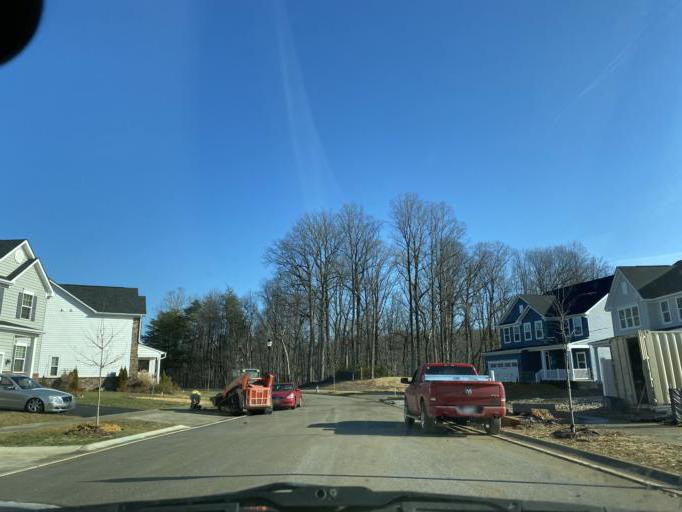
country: US
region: Maryland
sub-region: Montgomery County
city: Burtonsville
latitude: 39.0987
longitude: -76.9184
